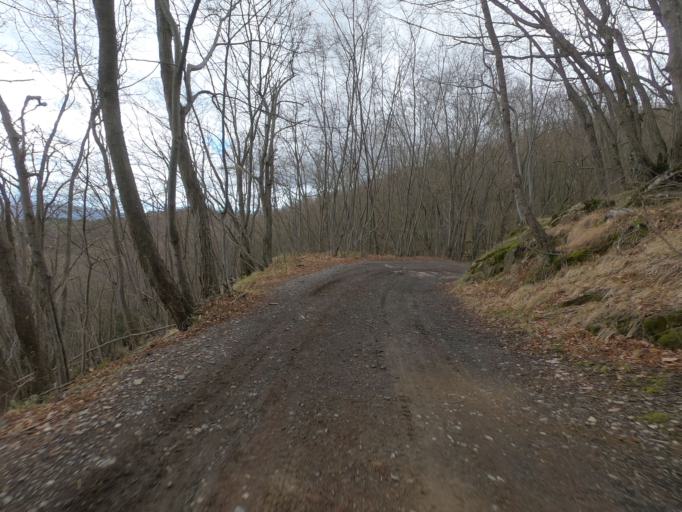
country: IT
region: Liguria
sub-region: Provincia di Imperia
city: Pietrabruna
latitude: 43.9127
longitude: 7.8898
